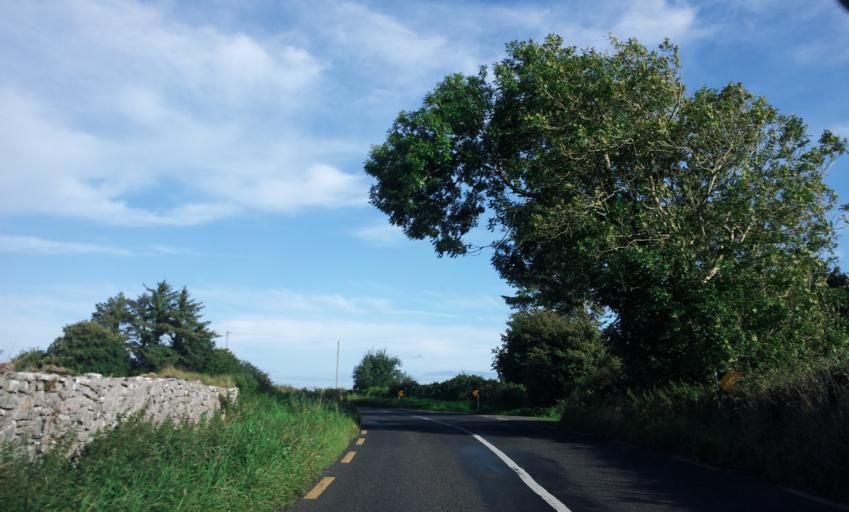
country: IE
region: Munster
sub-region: An Clar
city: Ennis
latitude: 52.9808
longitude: -9.1221
